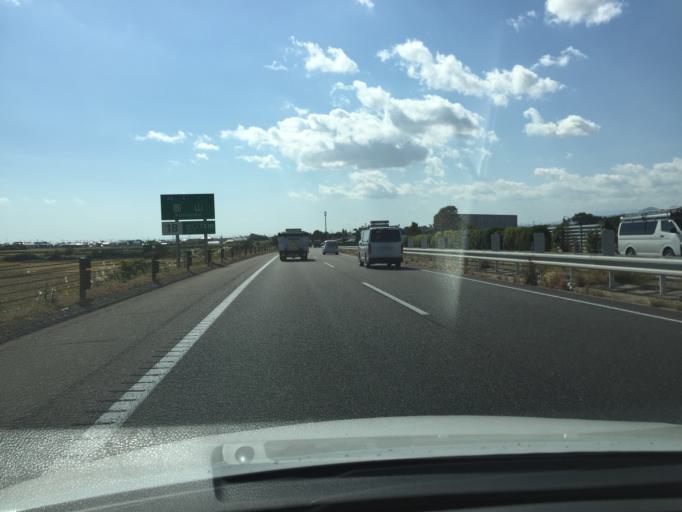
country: JP
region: Fukushima
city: Koriyama
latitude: 37.4443
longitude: 140.3517
